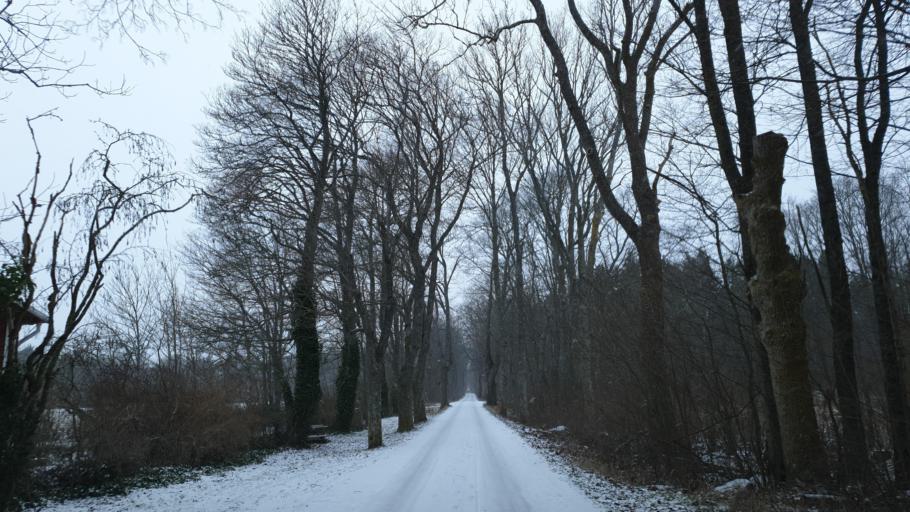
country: SE
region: Gotland
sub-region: Gotland
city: Visby
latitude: 57.5211
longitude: 18.4521
